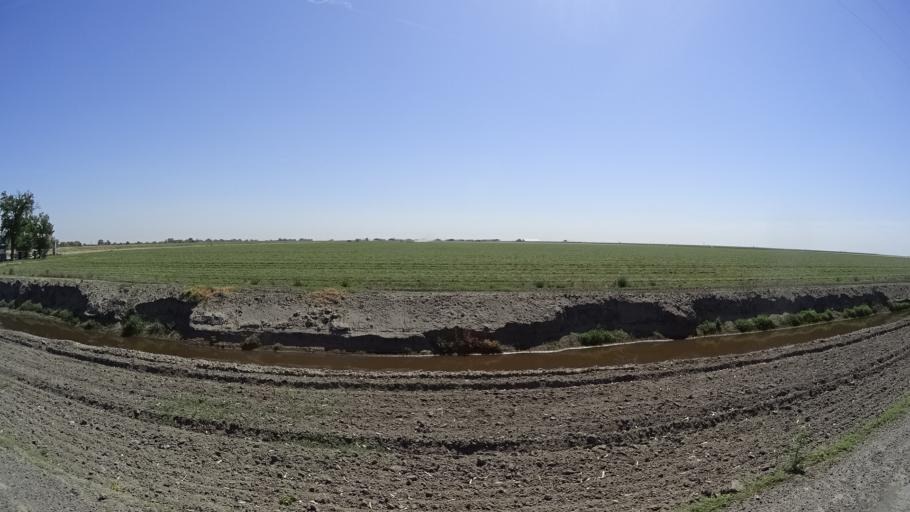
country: US
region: California
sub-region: Kings County
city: Corcoran
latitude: 36.0343
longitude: -119.5361
